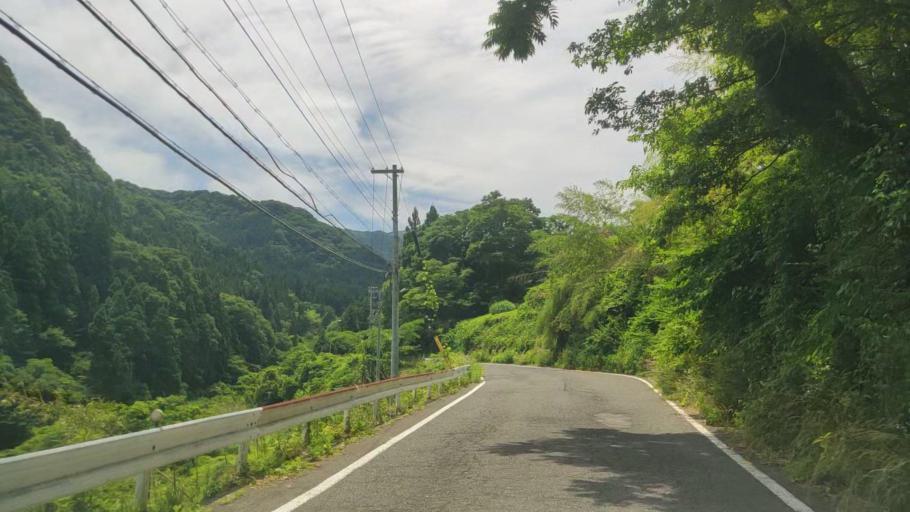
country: JP
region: Tottori
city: Tottori
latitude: 35.4378
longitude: 134.5324
